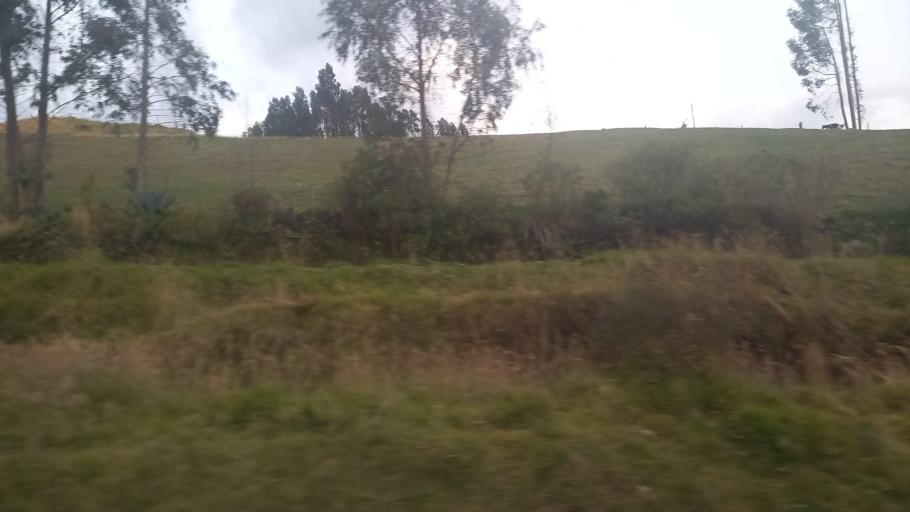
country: EC
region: Pichincha
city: Cayambe
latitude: 0.0866
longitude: -78.1020
